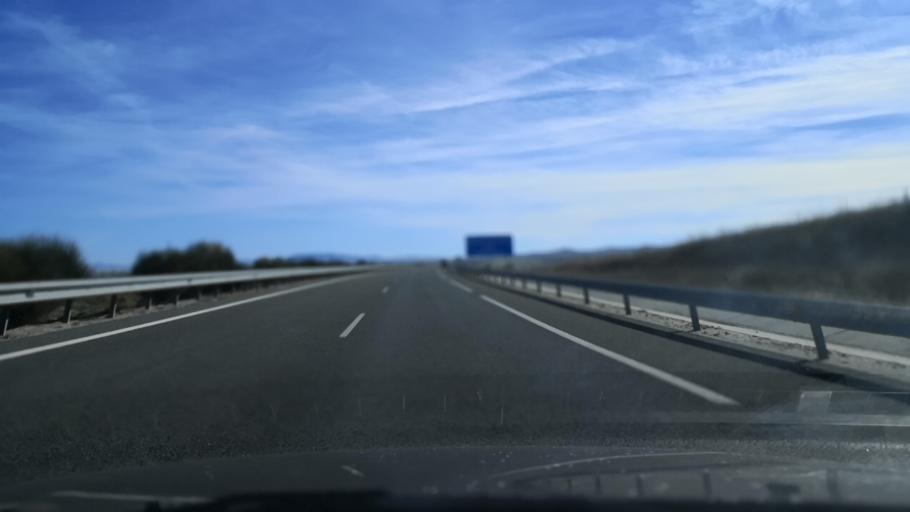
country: ES
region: Castille and Leon
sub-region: Provincia de Avila
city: Monsalupe
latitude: 40.8114
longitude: -4.7965
